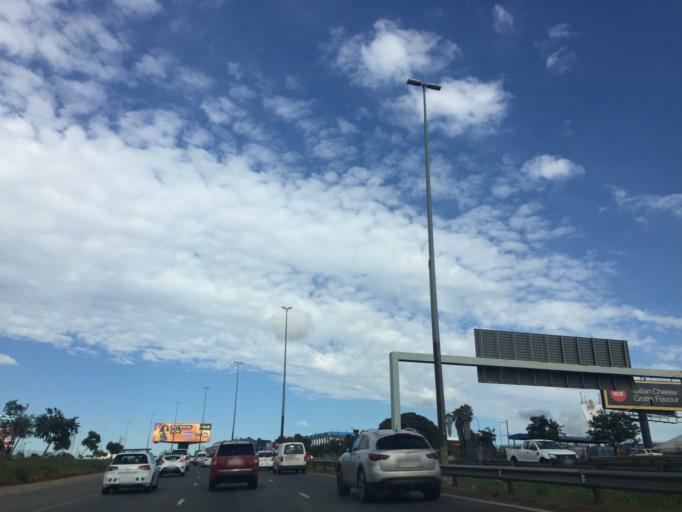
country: ZA
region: Gauteng
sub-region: City of Johannesburg Metropolitan Municipality
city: Modderfontein
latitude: -26.1294
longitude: 28.2138
